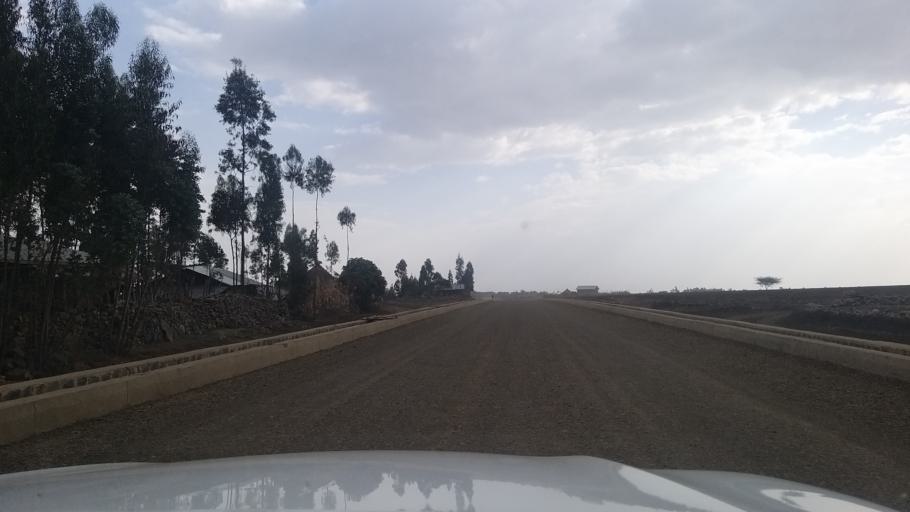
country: ET
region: Amhara
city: Were Ilu
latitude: 10.4479
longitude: 39.2011
